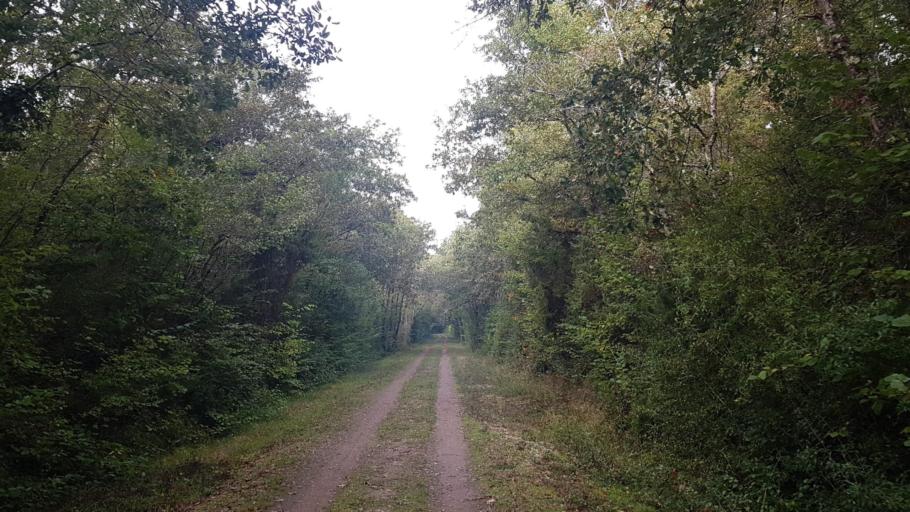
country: FR
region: Poitou-Charentes
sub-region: Departement de la Vienne
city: Saint-Savin
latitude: 46.5828
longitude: 0.8878
